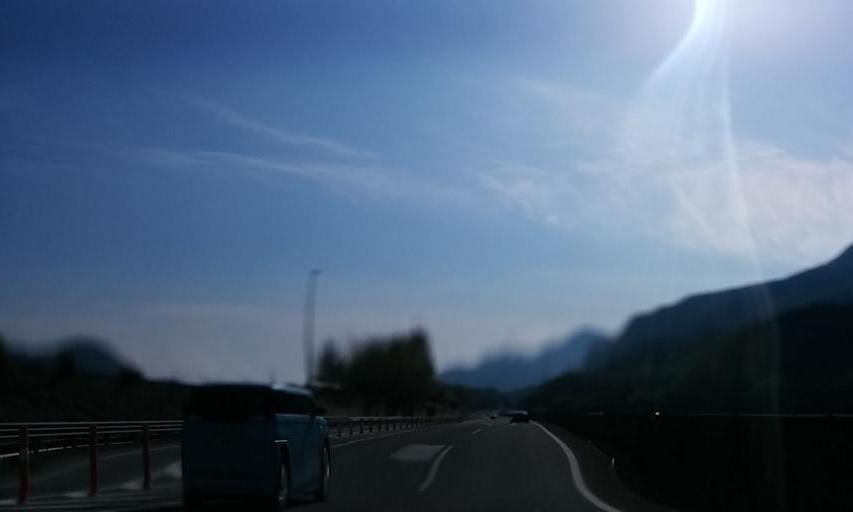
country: JP
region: Shiga Prefecture
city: Nagahama
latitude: 35.3180
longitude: 136.3238
